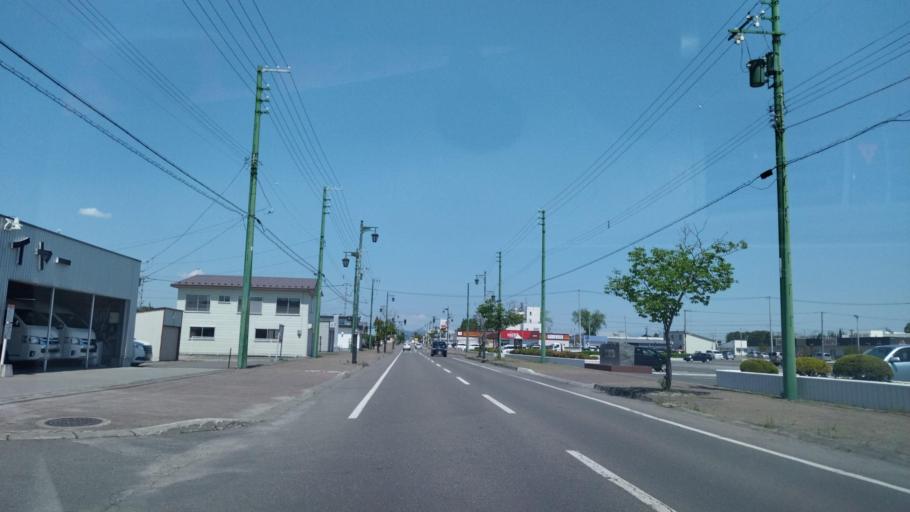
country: JP
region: Hokkaido
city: Otofuke
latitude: 43.1634
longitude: 143.2447
